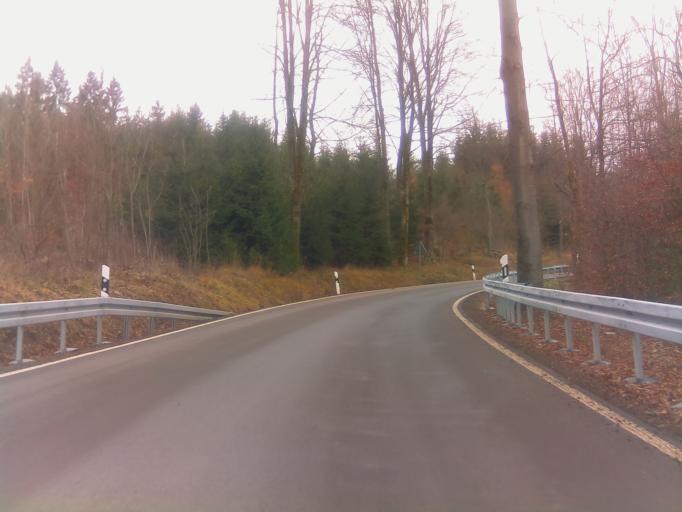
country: DE
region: Thuringia
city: Brotterode
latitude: 50.8174
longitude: 10.4629
